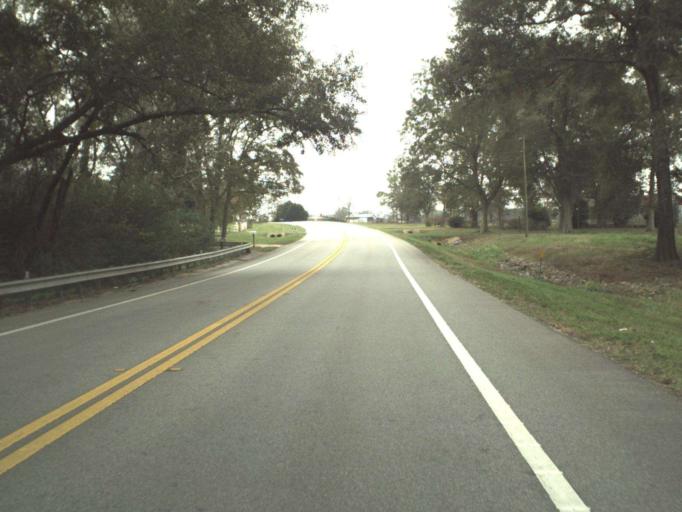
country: US
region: Alabama
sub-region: Escambia County
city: Atmore
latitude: 30.8763
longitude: -87.4453
